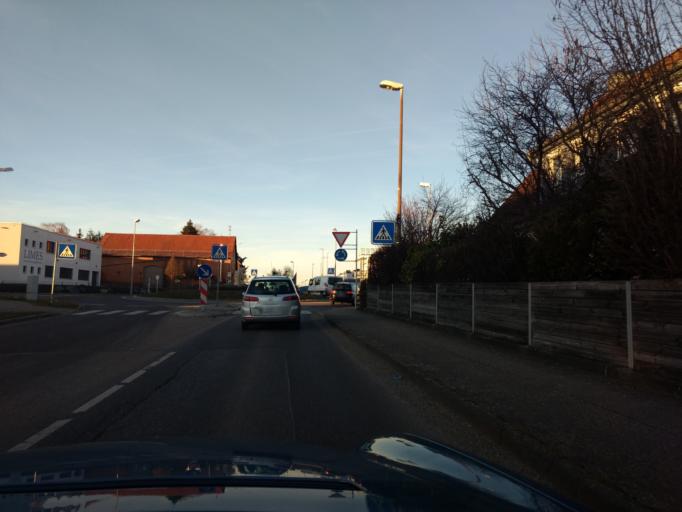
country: DE
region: Baden-Wuerttemberg
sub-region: Regierungsbezirk Stuttgart
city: Schwabisch Gmund
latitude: 48.7850
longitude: 9.7981
